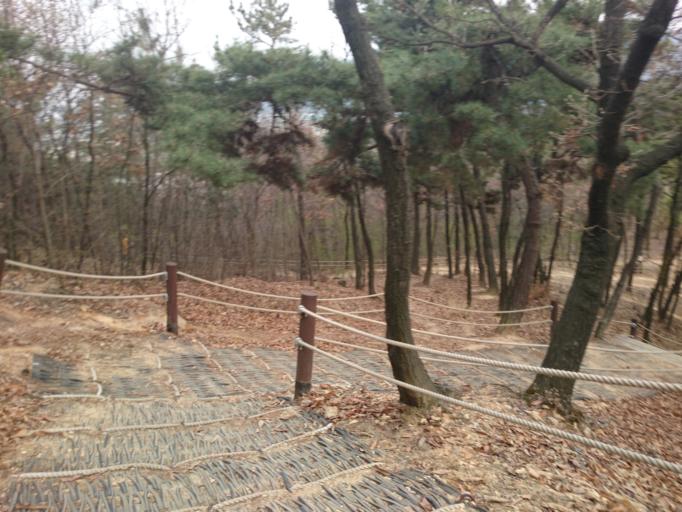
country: KR
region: Daegu
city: Daegu
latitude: 35.8461
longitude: 128.5564
